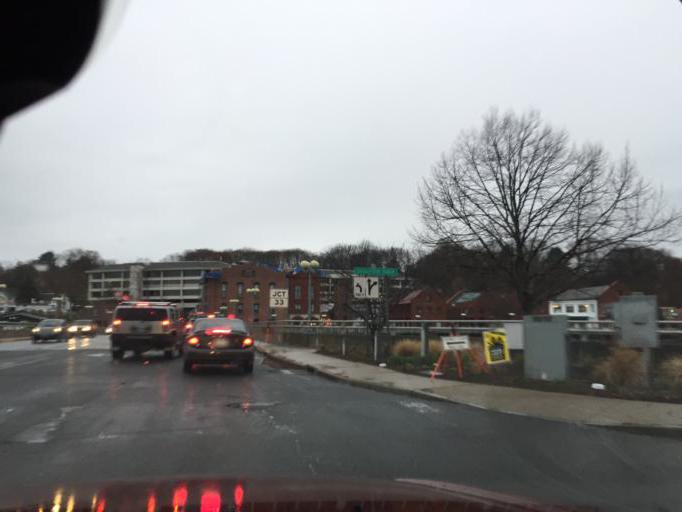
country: US
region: Connecticut
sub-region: Fairfield County
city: Westport
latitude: 41.1412
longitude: -73.3623
